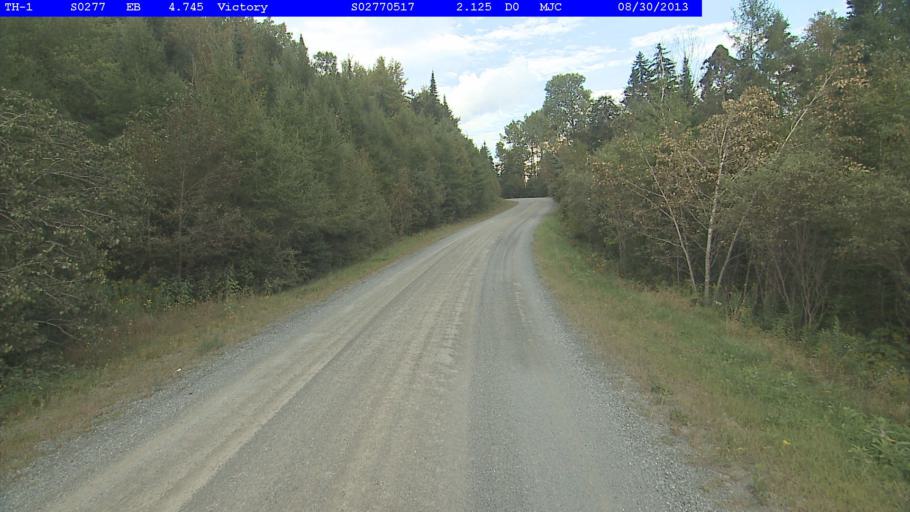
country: US
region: Vermont
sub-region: Caledonia County
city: Lyndonville
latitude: 44.5167
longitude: -71.8251
